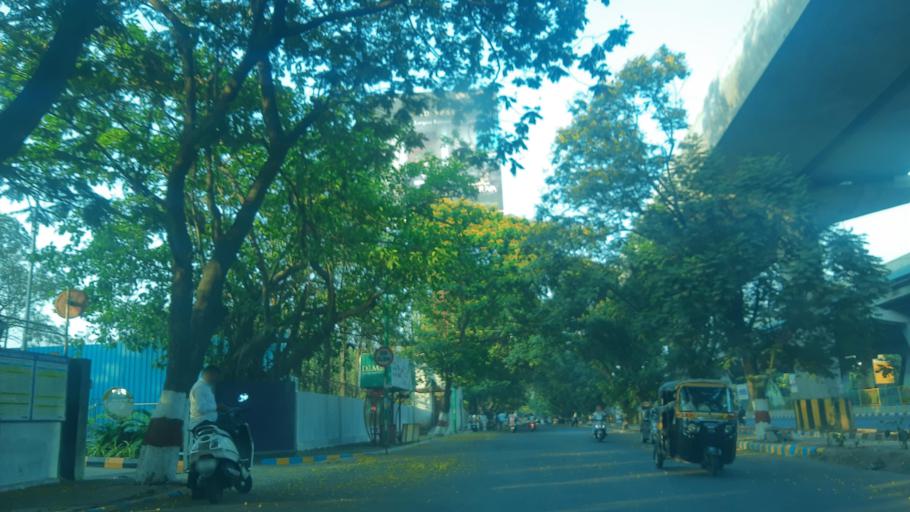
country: IN
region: Maharashtra
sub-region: Thane
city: Thane
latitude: 19.2030
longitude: 72.9667
